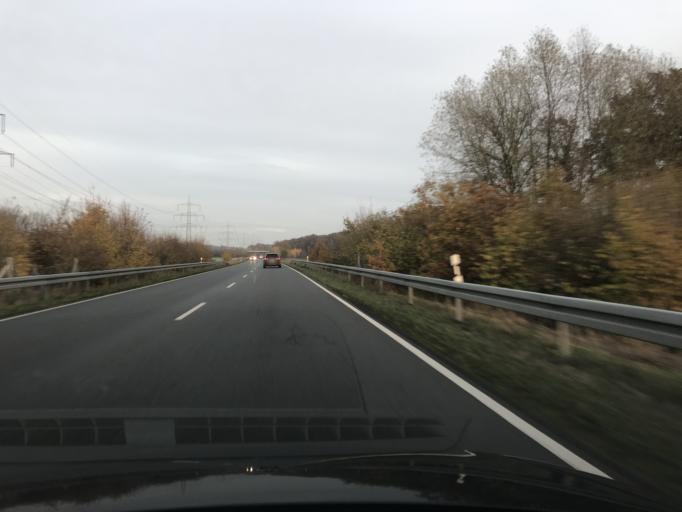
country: DE
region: North Rhine-Westphalia
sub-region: Regierungsbezirk Arnsberg
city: Hamm
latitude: 51.7209
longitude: 7.7684
